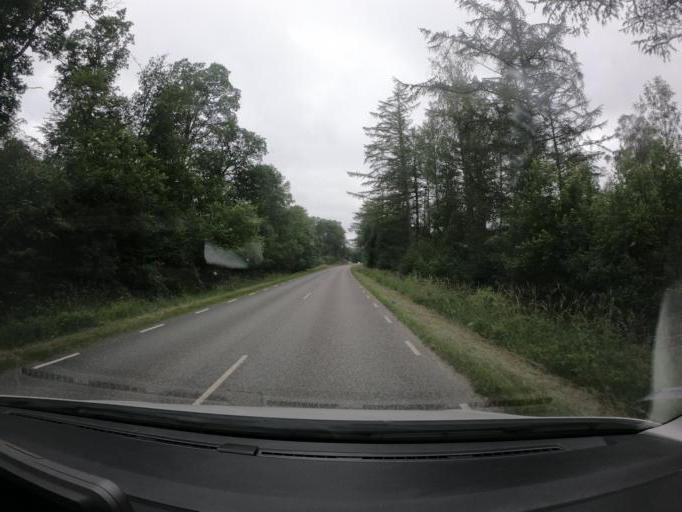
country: SE
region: Skane
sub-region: Perstorps Kommun
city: Perstorp
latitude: 56.1214
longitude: 13.4059
